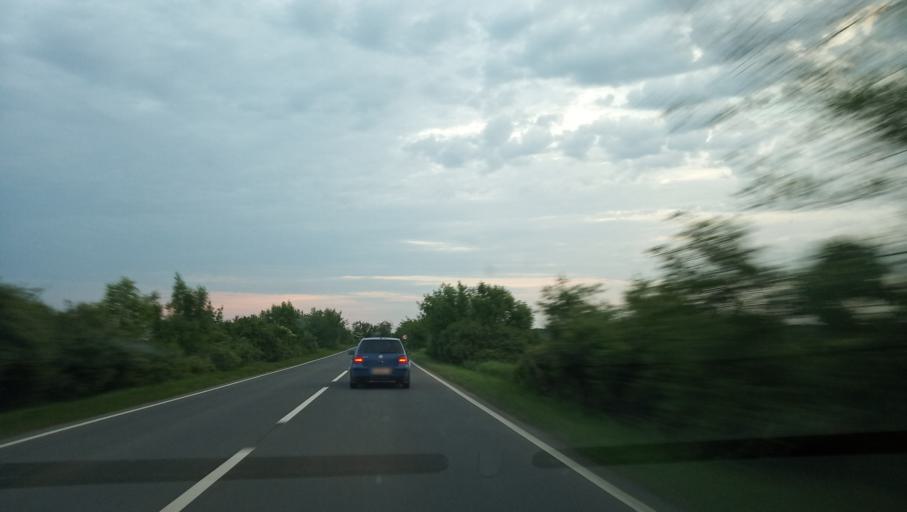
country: RO
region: Timis
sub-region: Comuna Padureni
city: Padureni
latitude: 45.6111
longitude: 21.1955
